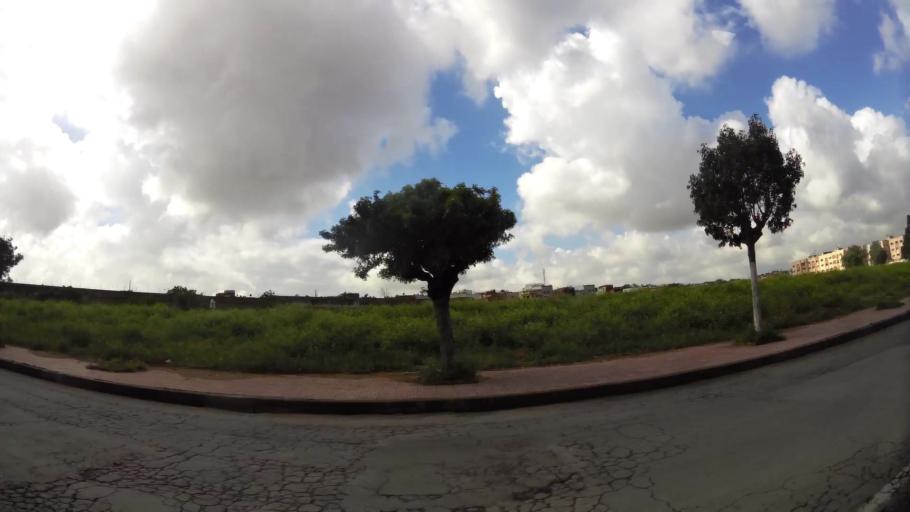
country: MA
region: Grand Casablanca
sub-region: Casablanca
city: Casablanca
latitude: 33.5491
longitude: -7.5931
